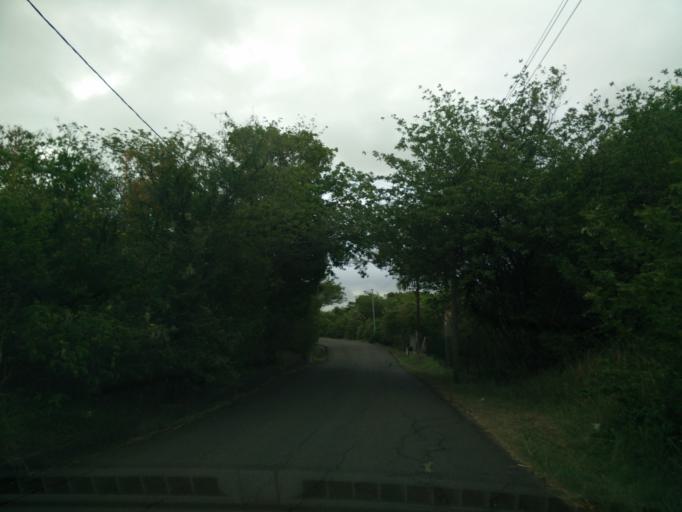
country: MQ
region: Martinique
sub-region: Martinique
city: Le Marin
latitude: 14.4468
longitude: -60.8366
